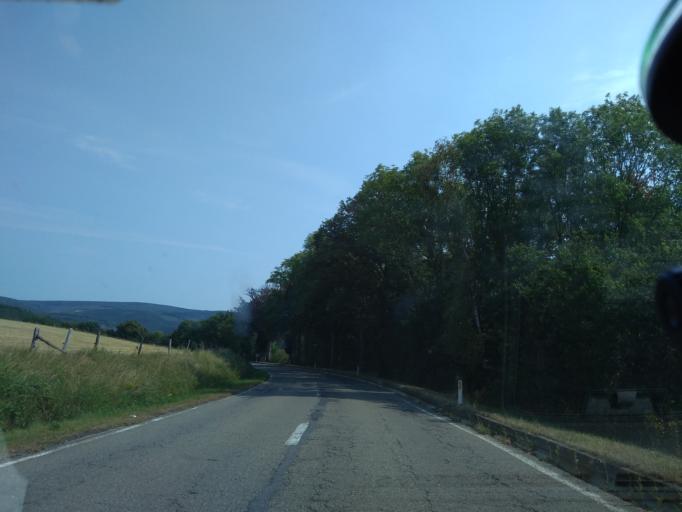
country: BE
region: Wallonia
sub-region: Province du Luxembourg
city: La Roche-en-Ardenne
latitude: 50.1639
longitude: 5.5598
